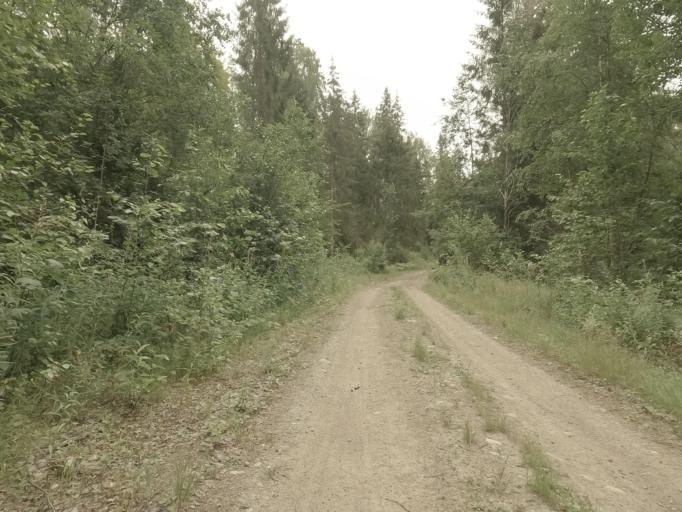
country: RU
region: Leningrad
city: Kamennogorsk
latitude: 61.0683
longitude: 29.1667
